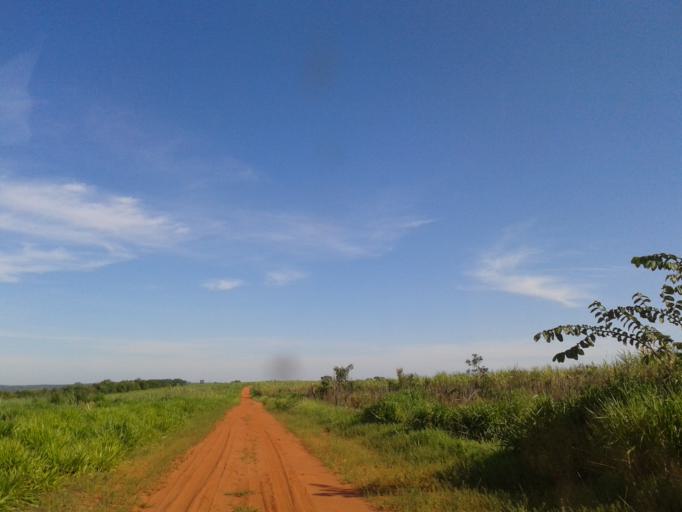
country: BR
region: Minas Gerais
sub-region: Santa Vitoria
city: Santa Vitoria
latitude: -19.1077
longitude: -49.9896
